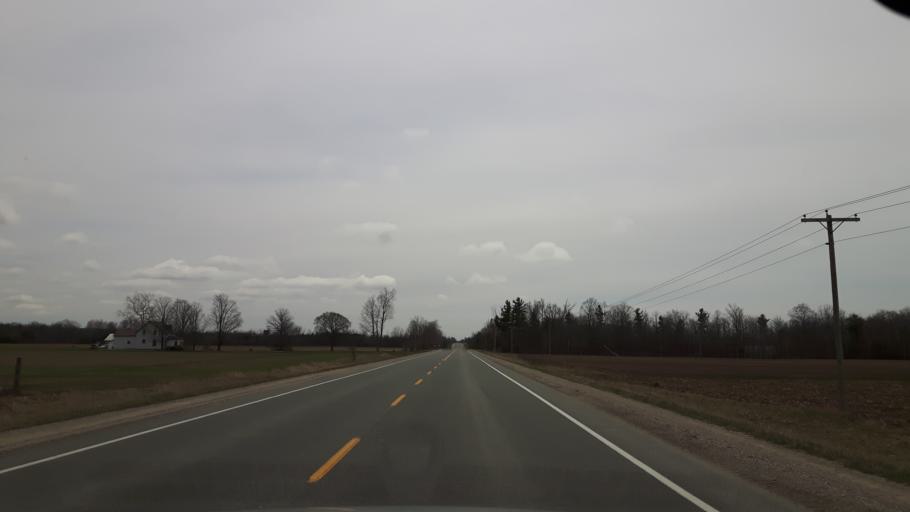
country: CA
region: Ontario
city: Goderich
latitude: 43.6193
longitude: -81.7057
